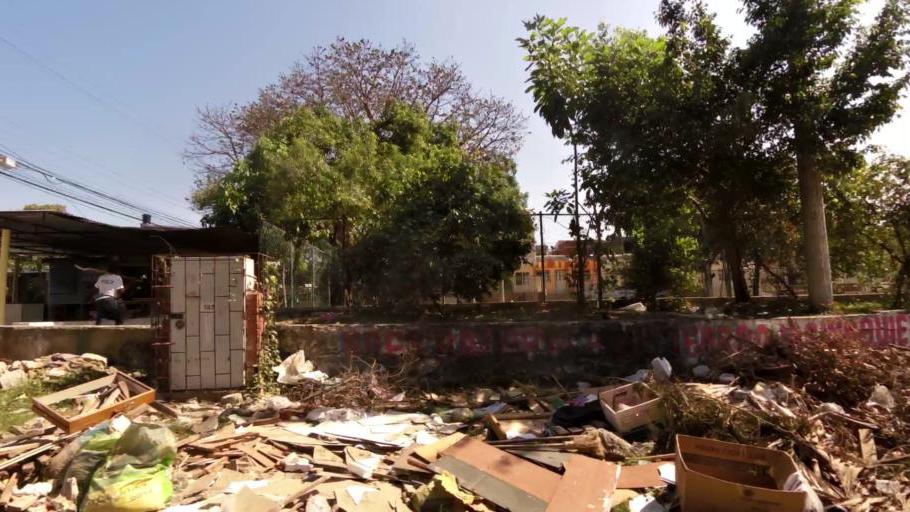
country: CO
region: Bolivar
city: Cartagena
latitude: 10.3923
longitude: -75.5069
